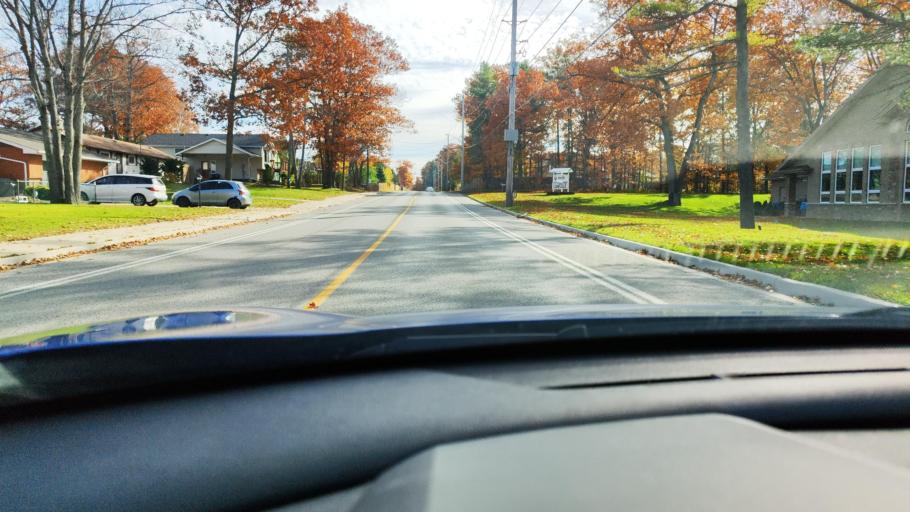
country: CA
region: Ontario
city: Wasaga Beach
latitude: 44.5231
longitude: -79.9990
